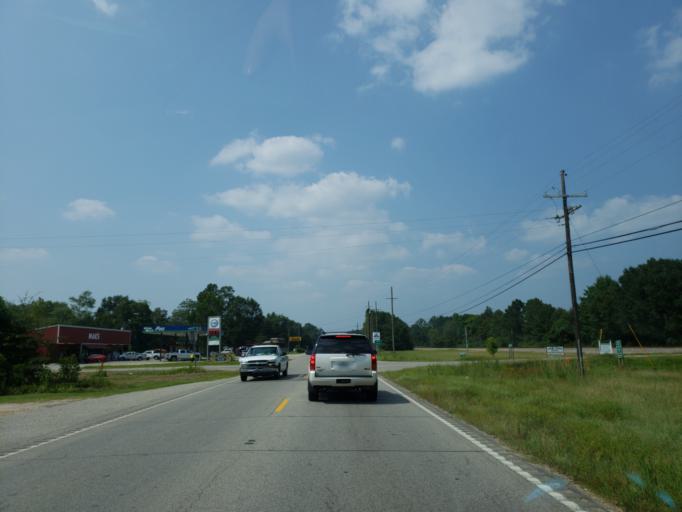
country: US
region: Mississippi
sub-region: Forrest County
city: Glendale
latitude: 31.4333
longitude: -89.2836
